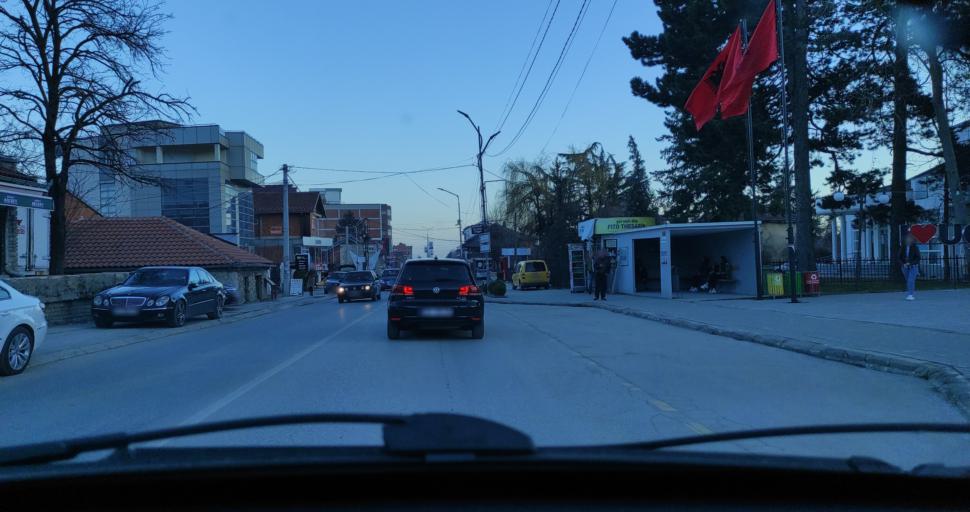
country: XK
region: Gjakova
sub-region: Komuna e Decanit
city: Decan
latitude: 42.5397
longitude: 20.2886
